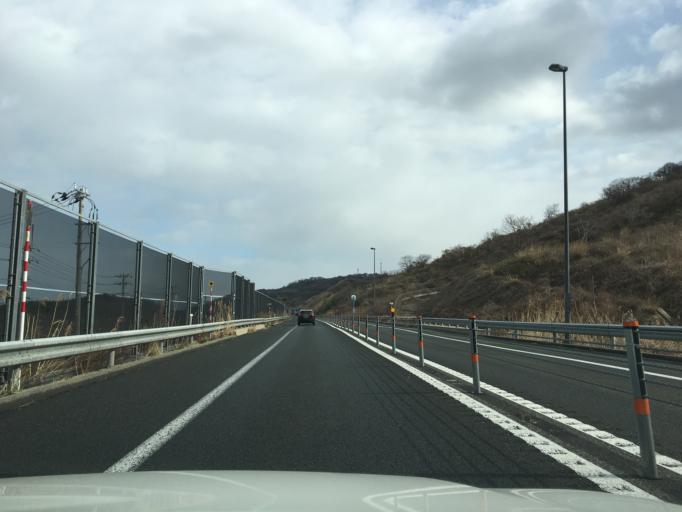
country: JP
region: Yamagata
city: Yuza
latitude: 39.3084
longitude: 139.9823
